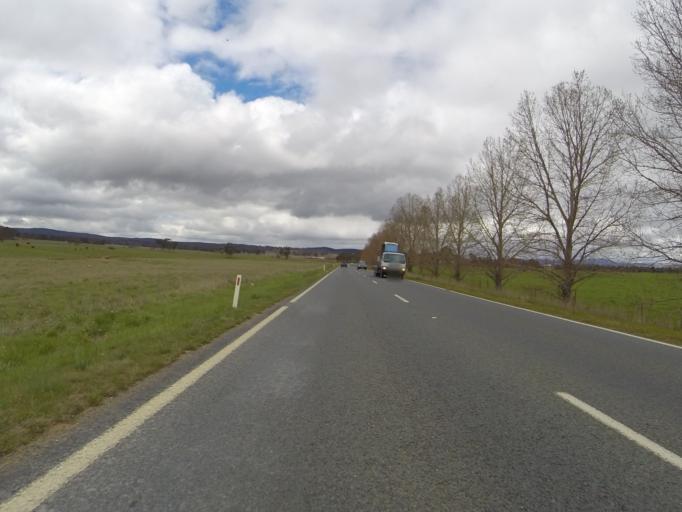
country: AU
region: Australian Capital Territory
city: Canberra
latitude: -35.2610
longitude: 149.1927
